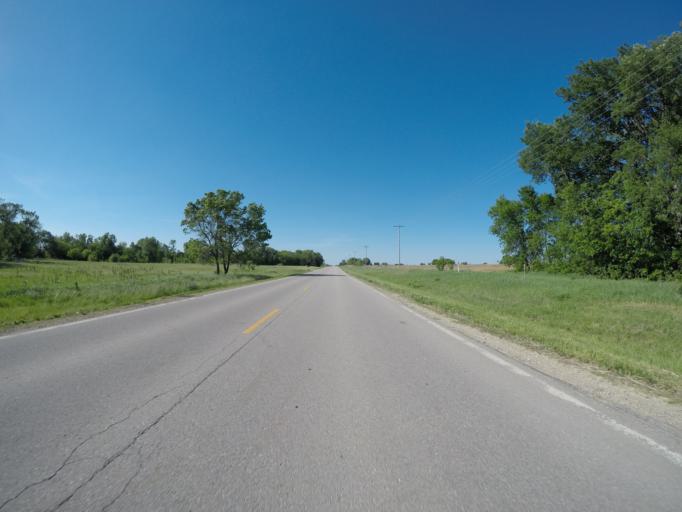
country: US
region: Kansas
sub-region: Riley County
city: Fort Riley North
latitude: 39.3083
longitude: -96.8308
